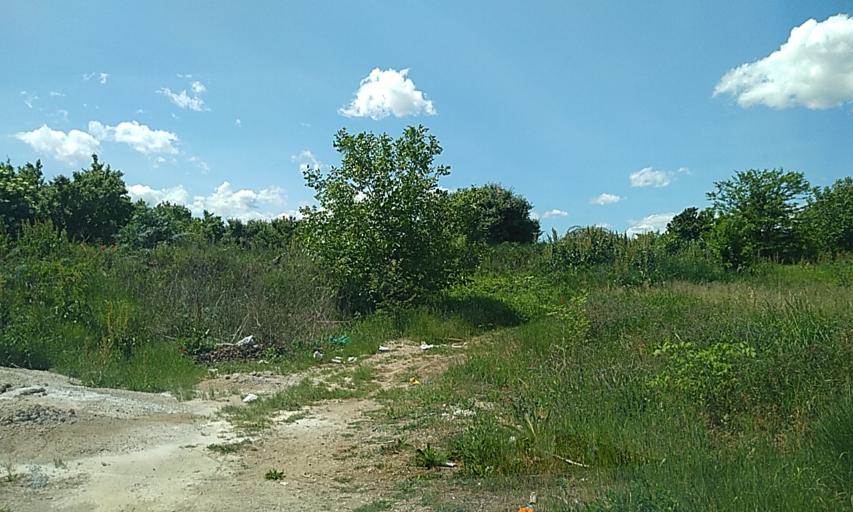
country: RS
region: Central Serbia
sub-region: Nisavski Okrug
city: Nis
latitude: 43.3370
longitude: 21.9044
